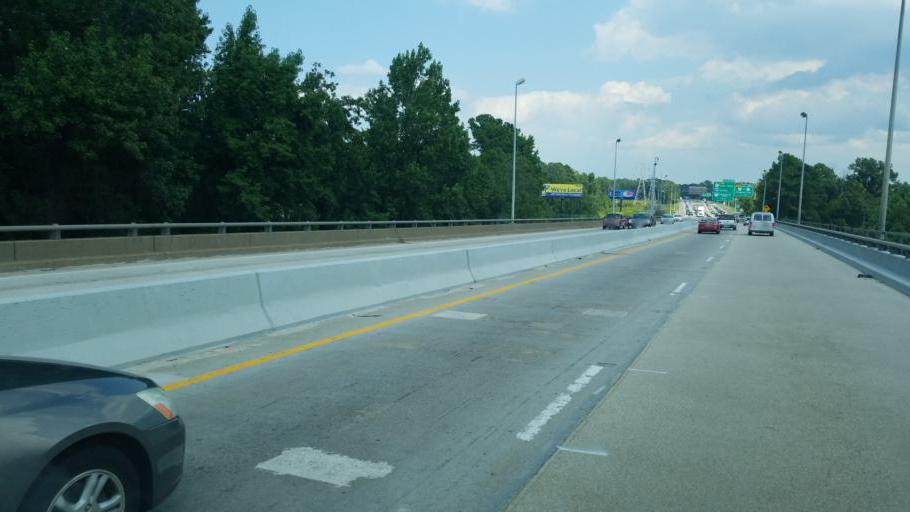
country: US
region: Virginia
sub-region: City of Chesapeake
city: Chesapeake
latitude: 36.7575
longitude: -76.2895
